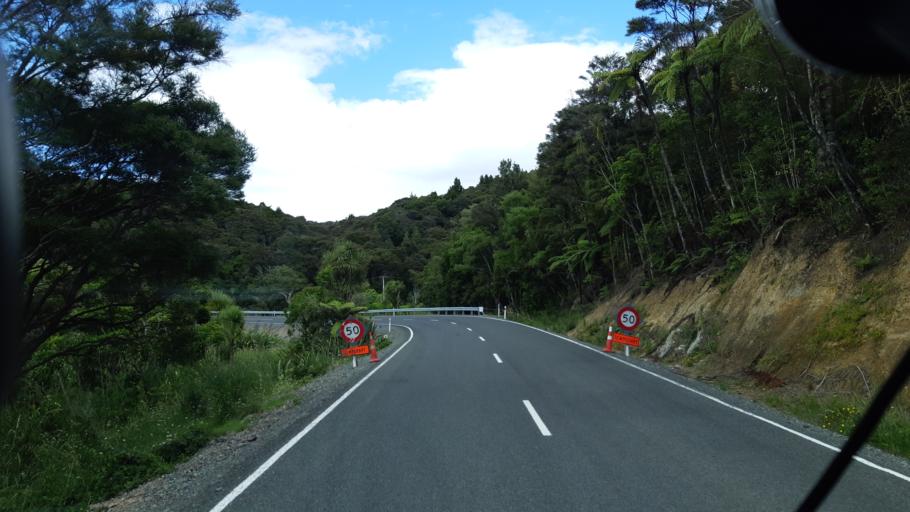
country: NZ
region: Northland
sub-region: Far North District
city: Taipa
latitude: -35.2426
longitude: 173.5358
